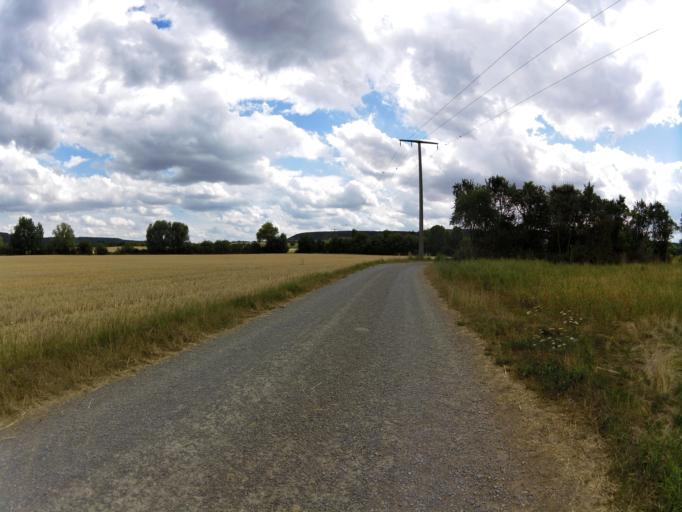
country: DE
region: Bavaria
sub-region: Regierungsbezirk Unterfranken
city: Zellingen
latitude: 49.8867
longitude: 9.8202
